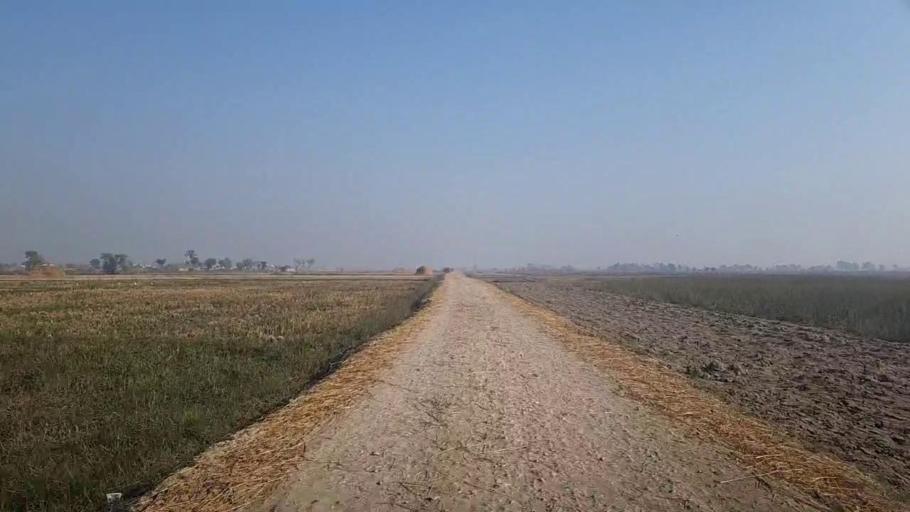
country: PK
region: Sindh
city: Radhan
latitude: 27.1408
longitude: 67.9078
